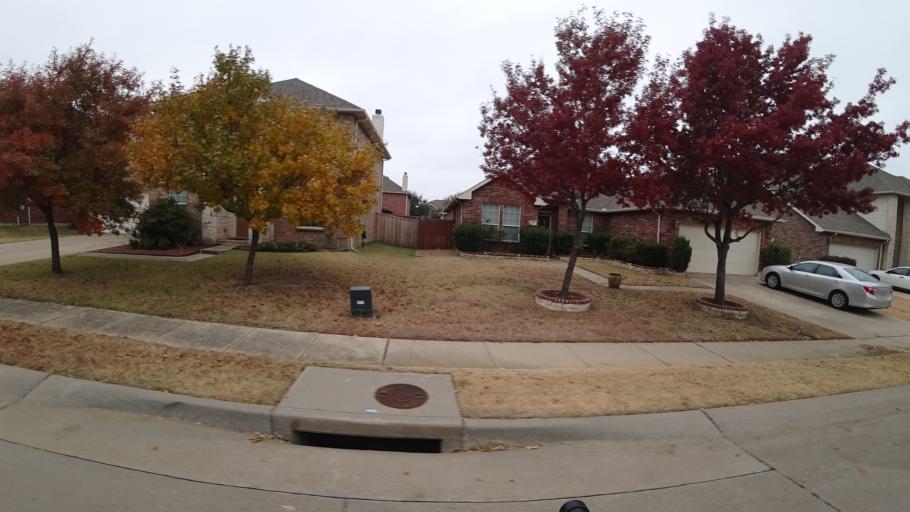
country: US
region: Texas
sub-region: Denton County
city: The Colony
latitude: 33.0656
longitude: -96.9019
